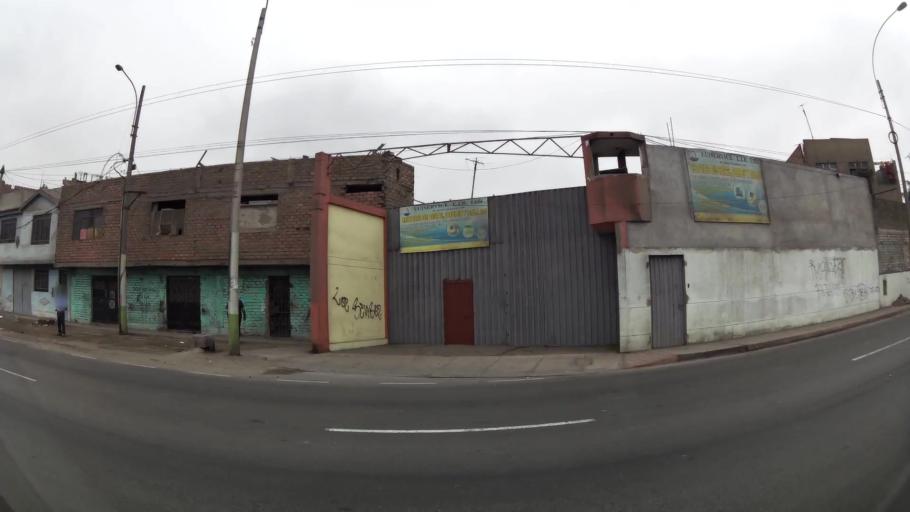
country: PE
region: Callao
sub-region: Callao
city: Callao
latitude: -12.0393
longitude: -77.1270
